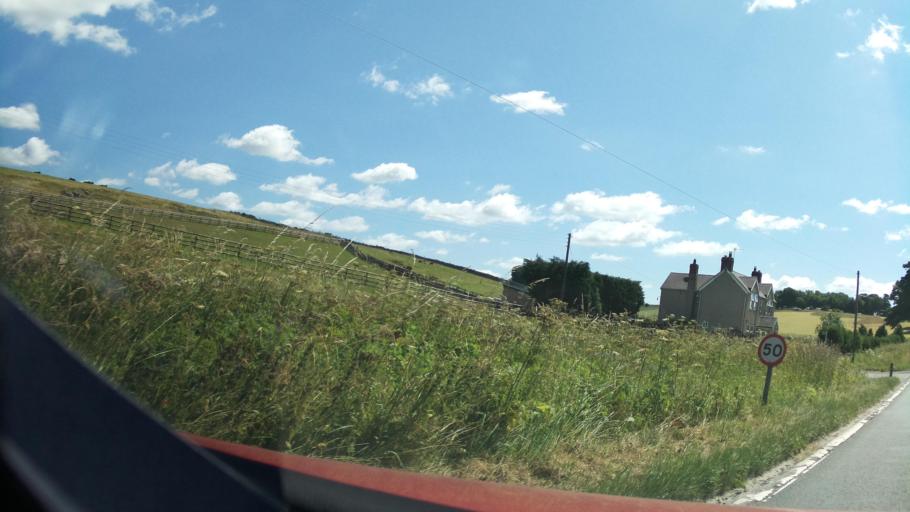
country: GB
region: England
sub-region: Derbyshire
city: Bakewell
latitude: 53.1306
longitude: -1.7549
